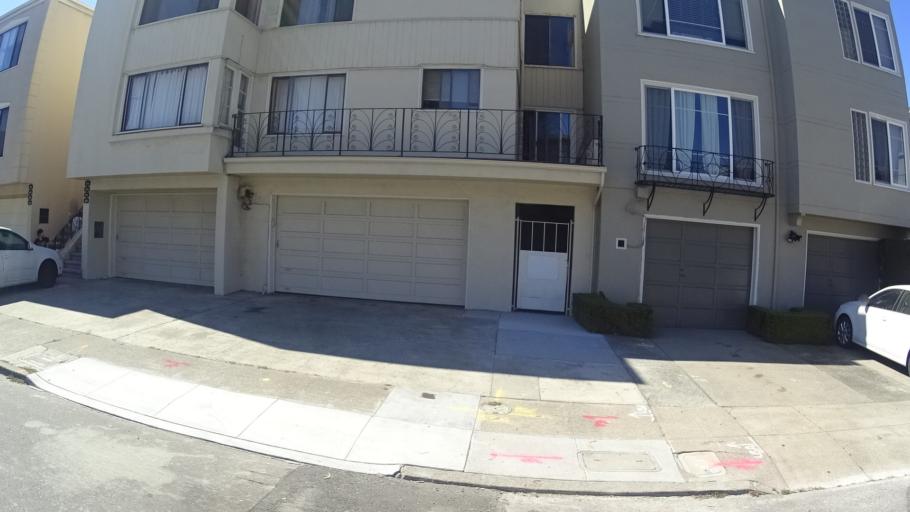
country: US
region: California
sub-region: San Francisco County
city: San Francisco
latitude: 37.7796
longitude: -122.4454
